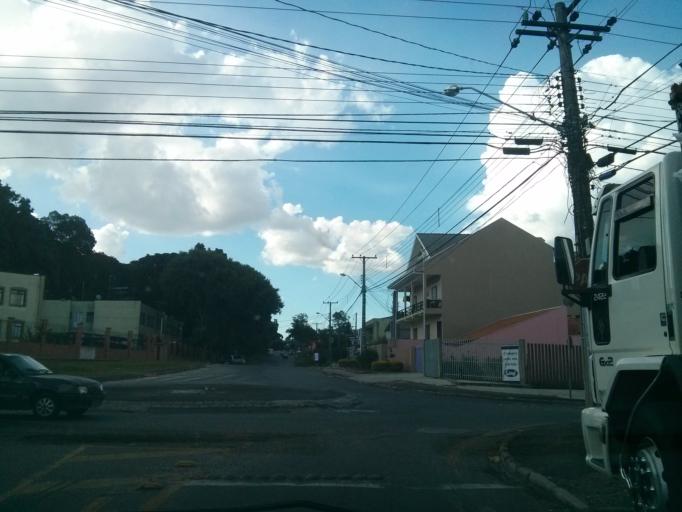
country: BR
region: Parana
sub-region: Sao Jose Dos Pinhais
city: Sao Jose dos Pinhais
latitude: -25.5258
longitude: -49.2381
